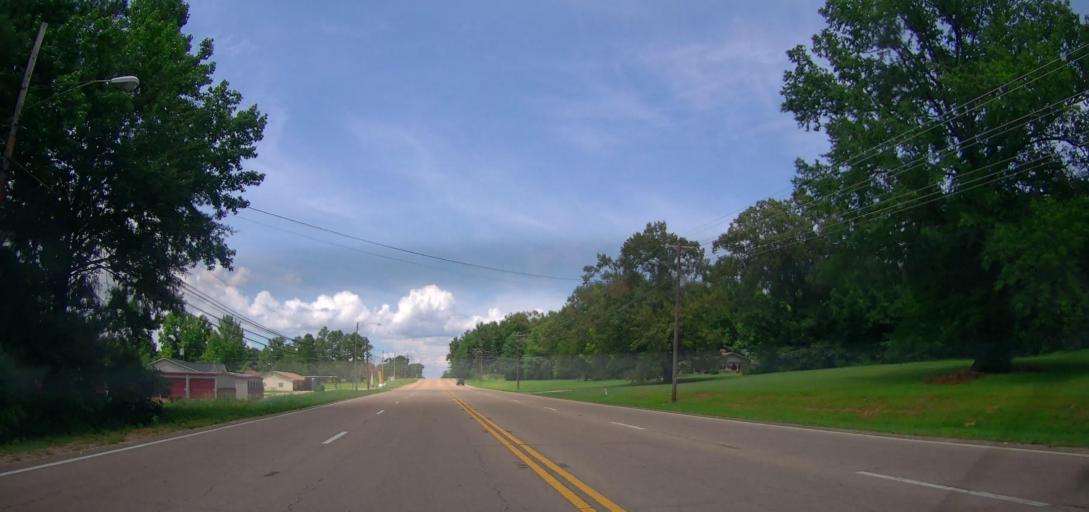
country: US
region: Mississippi
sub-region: Lee County
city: Verona
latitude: 34.1713
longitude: -88.7197
